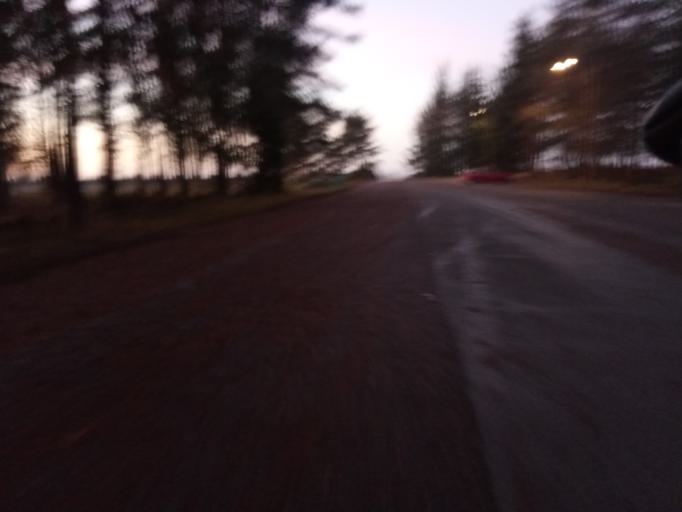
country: EE
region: Harju
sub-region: Kuusalu vald
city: Kuusalu
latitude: 59.4505
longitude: 25.4177
